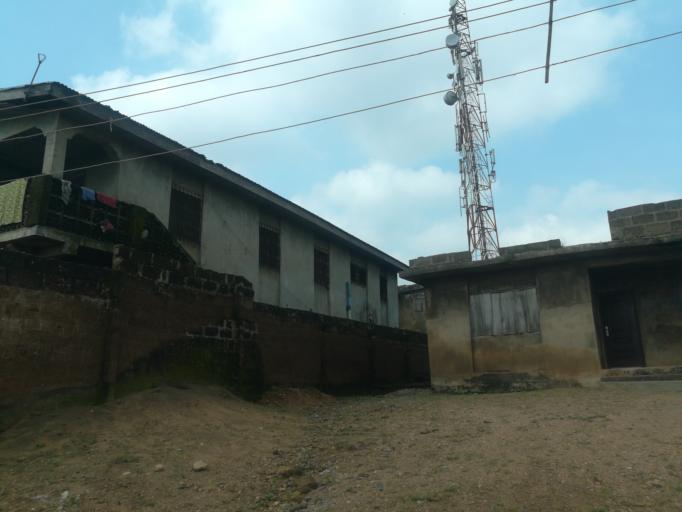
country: NG
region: Oyo
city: Ibadan
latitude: 7.4174
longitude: 3.9529
